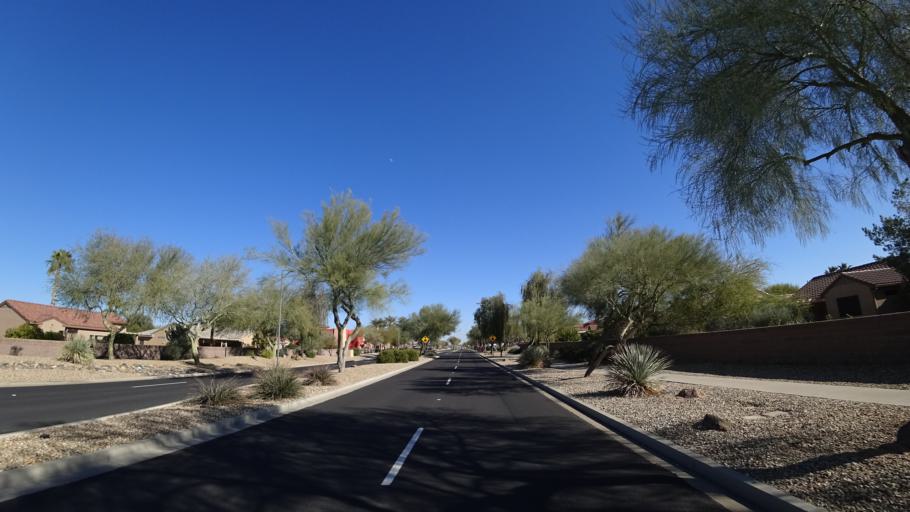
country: US
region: Arizona
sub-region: Maricopa County
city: Sun City West
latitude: 33.6550
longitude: -112.4064
